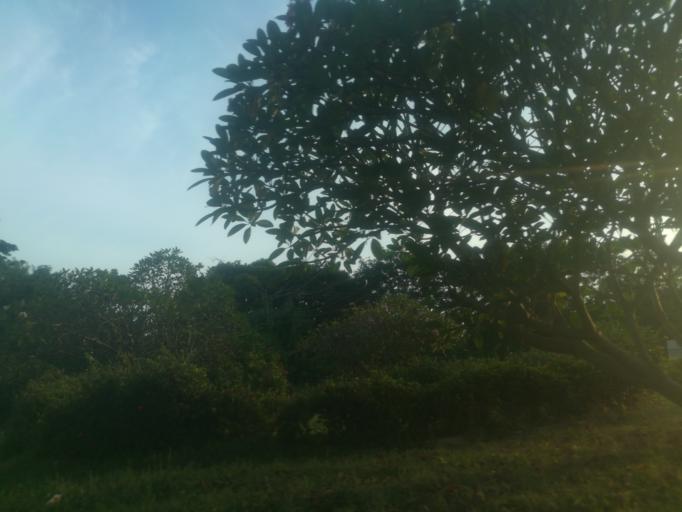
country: NG
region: Ogun
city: Abeokuta
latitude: 7.1350
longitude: 3.3433
